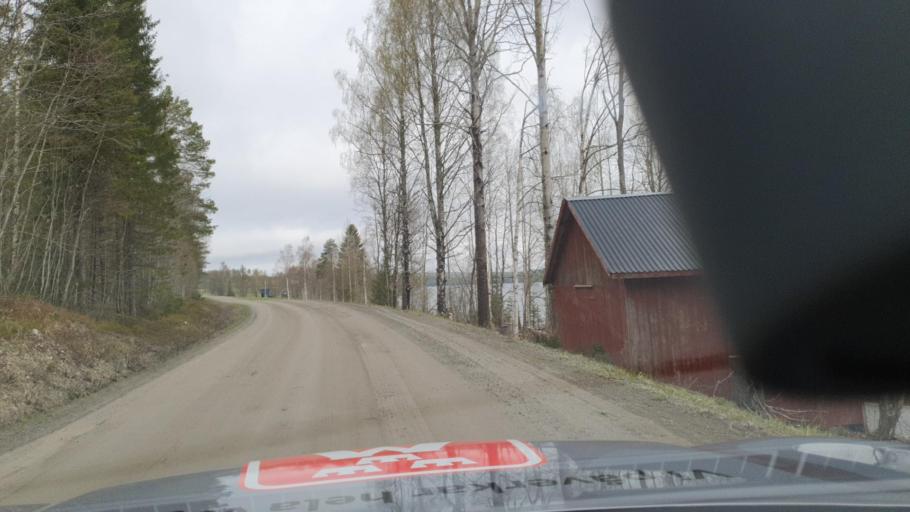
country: SE
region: Vaesternorrland
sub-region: OErnskoeldsviks Kommun
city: Husum
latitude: 63.6392
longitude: 19.0588
